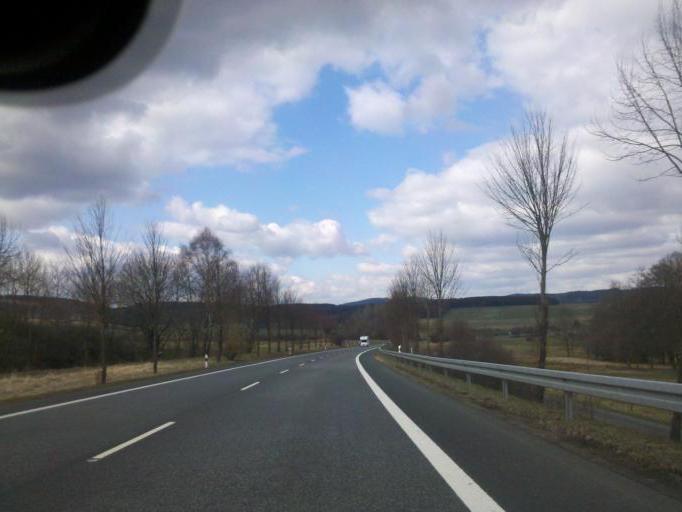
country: DE
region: Hesse
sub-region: Regierungsbezirk Giessen
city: Breidenbach
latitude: 50.8337
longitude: 8.3873
